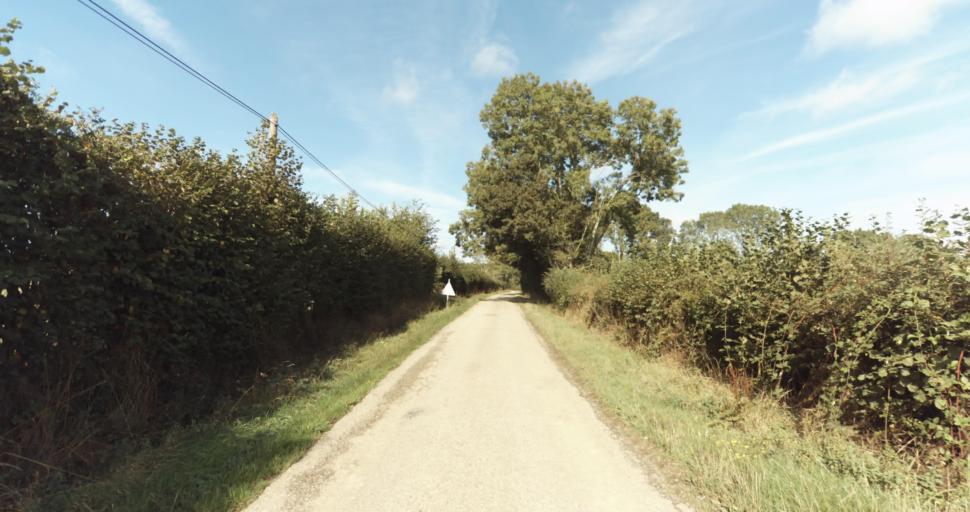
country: FR
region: Lower Normandy
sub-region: Departement du Calvados
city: La Vespiere
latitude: 48.9214
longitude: 0.3349
